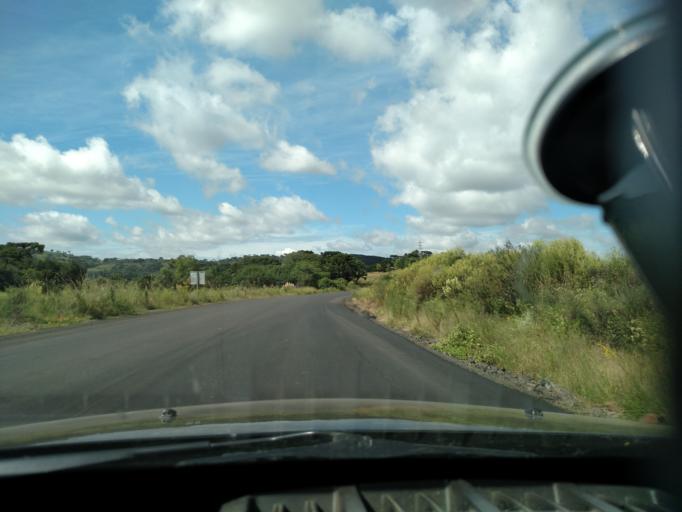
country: BR
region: Santa Catarina
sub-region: Sao Joaquim
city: Sao Joaquim
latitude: -28.1158
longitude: -50.0495
